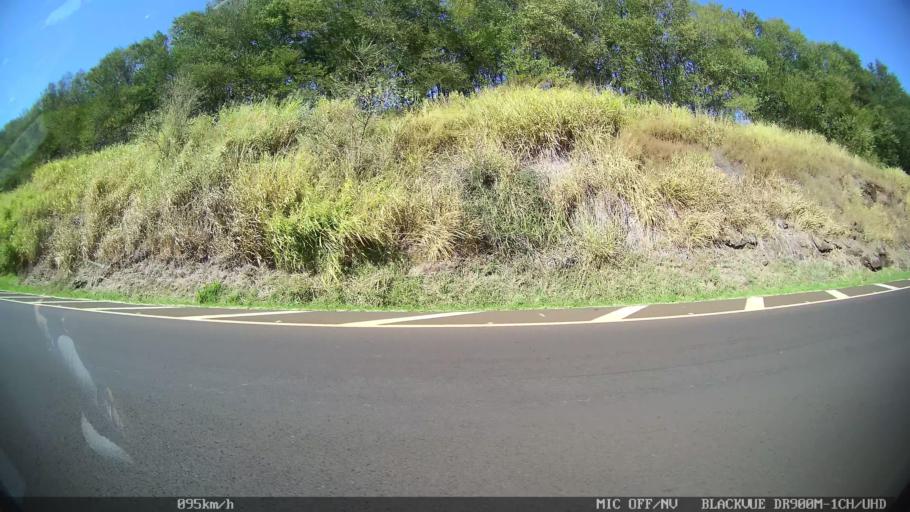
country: BR
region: Sao Paulo
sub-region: Franca
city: Franca
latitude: -20.5860
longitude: -47.4341
